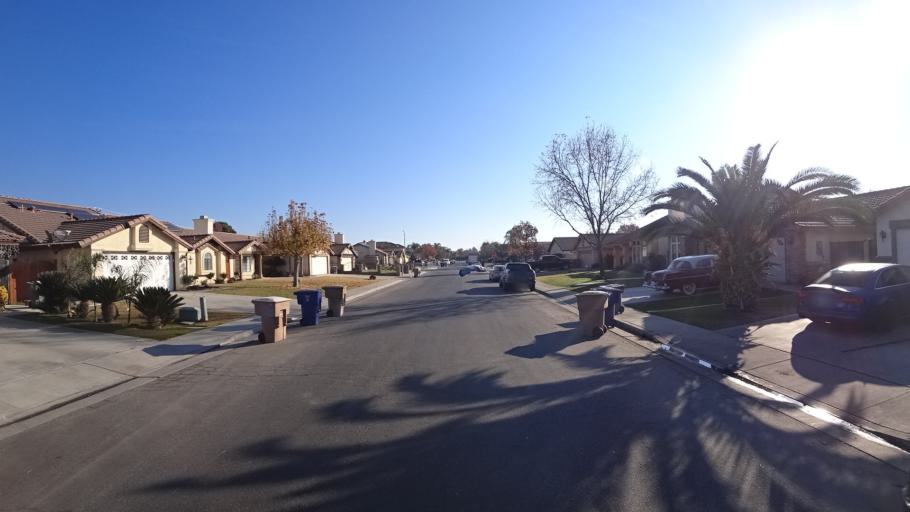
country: US
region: California
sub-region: Kern County
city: Greenfield
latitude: 35.3023
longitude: -119.0093
